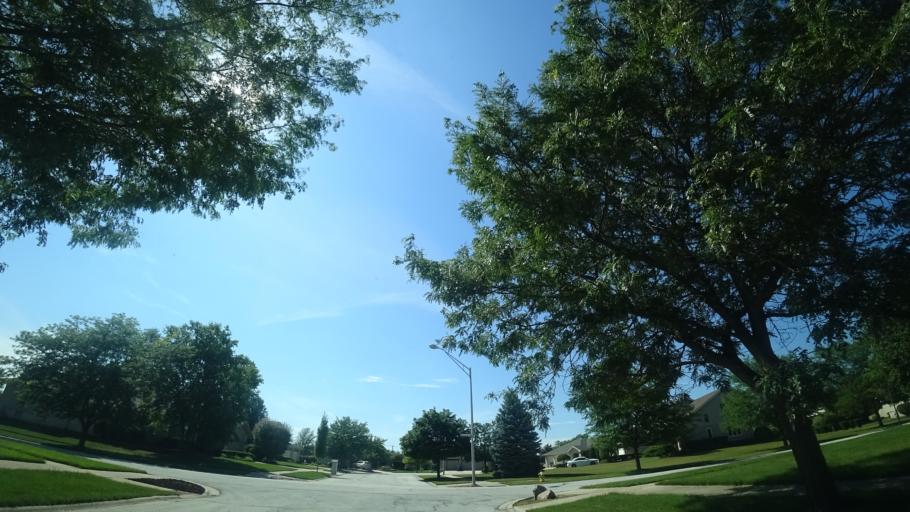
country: US
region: Illinois
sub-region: Will County
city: Homer Glen
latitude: 41.5705
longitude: -87.9080
